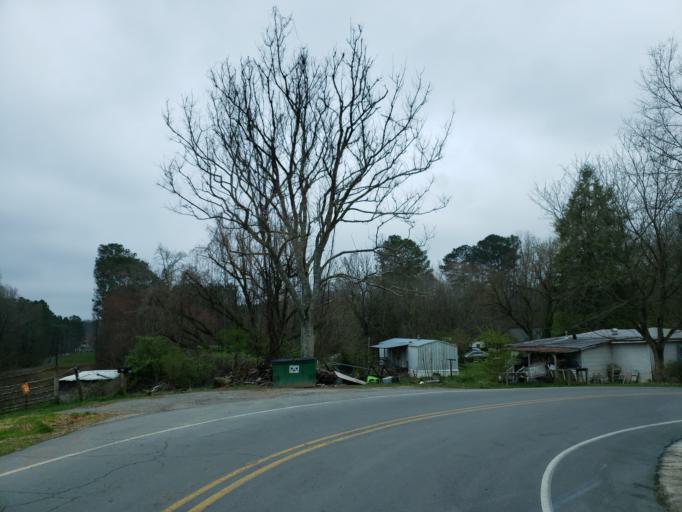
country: US
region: Georgia
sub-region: Pickens County
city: Jasper
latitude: 34.4603
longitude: -84.4219
